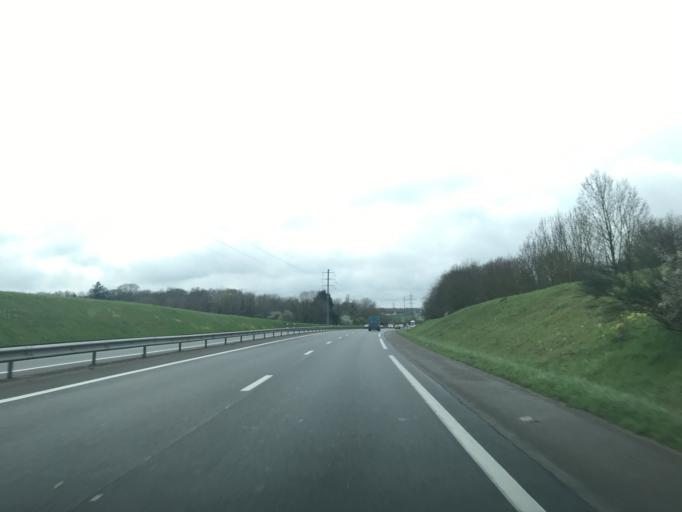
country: FR
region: Centre
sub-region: Departement du Loiret
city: Boigny-sur-Bionne
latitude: 47.9159
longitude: 2.0116
